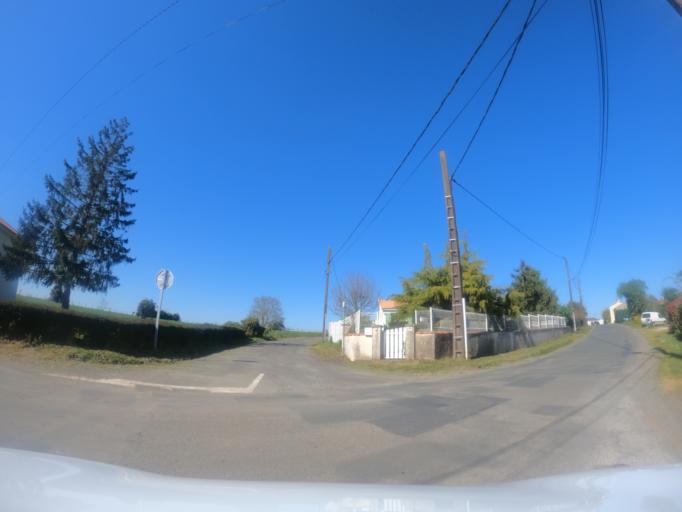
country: FR
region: Pays de la Loire
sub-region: Departement de la Vendee
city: Fontenay-le-Comte
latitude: 46.4262
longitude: -0.8155
